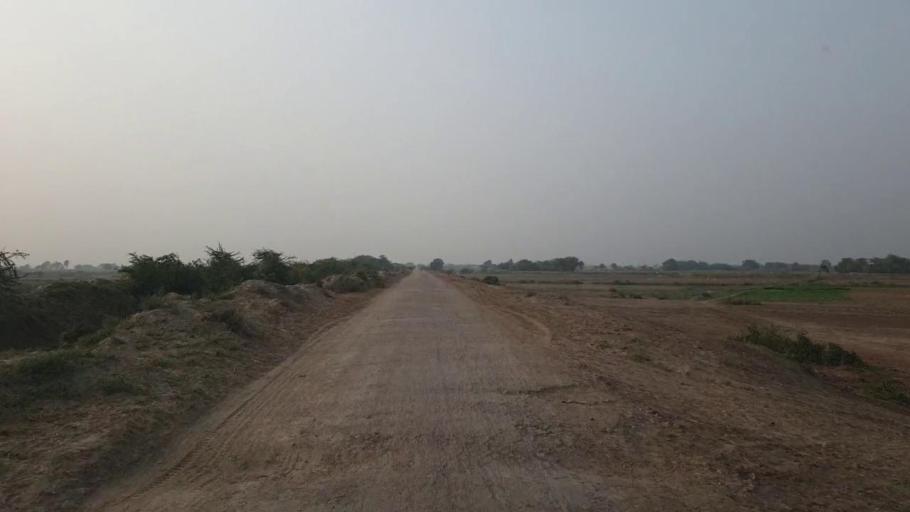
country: PK
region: Sindh
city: Mirpur Batoro
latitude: 24.6429
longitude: 68.3953
